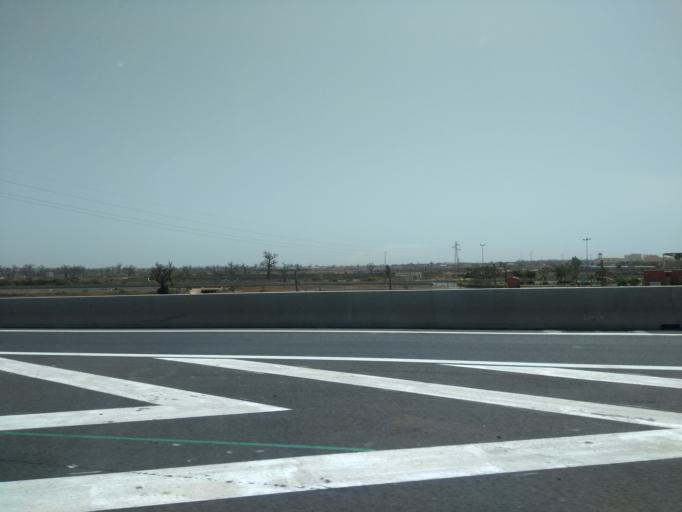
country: SN
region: Thies
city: Pout
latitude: 14.7301
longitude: -17.1580
